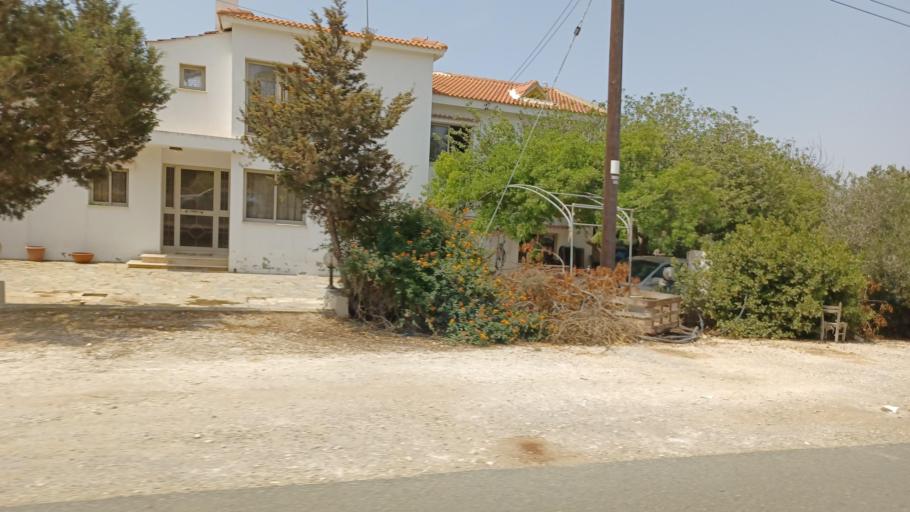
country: CY
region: Ammochostos
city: Ayia Napa
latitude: 34.9929
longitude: 34.0103
